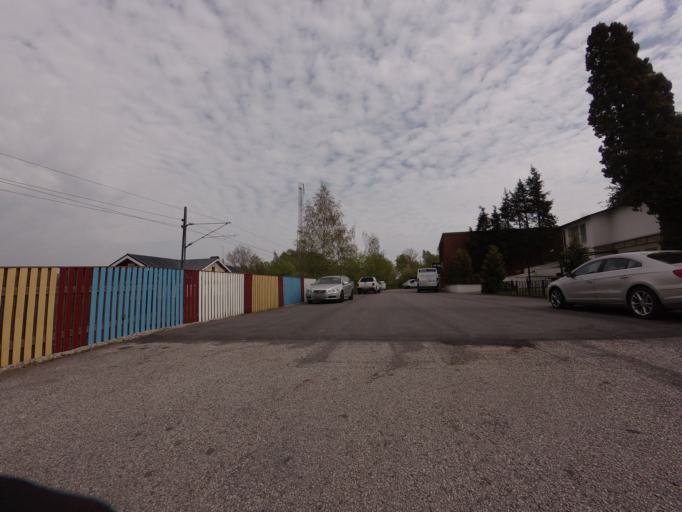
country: SE
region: Skane
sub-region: Malmo
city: Oxie
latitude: 55.5442
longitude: 13.0849
